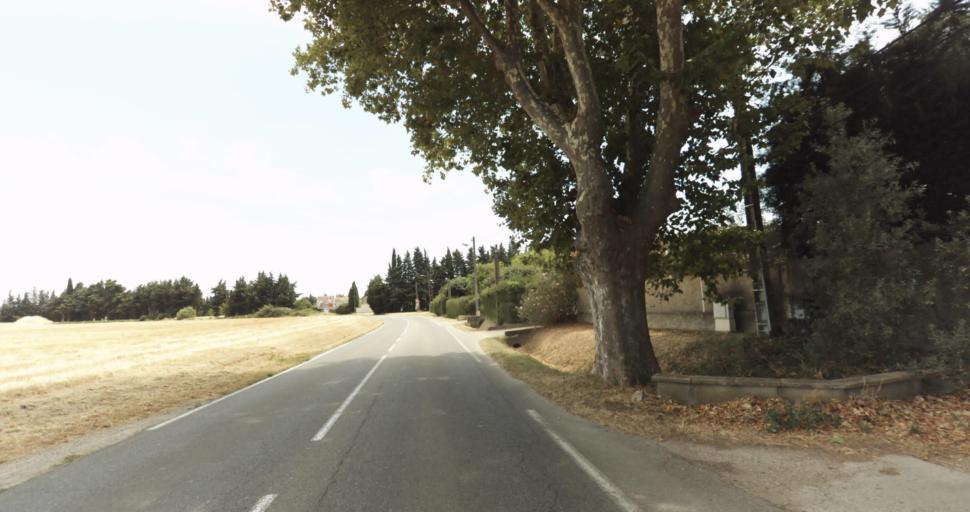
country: FR
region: Provence-Alpes-Cote d'Azur
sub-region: Departement du Vaucluse
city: Monteux
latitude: 44.0423
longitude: 4.9877
